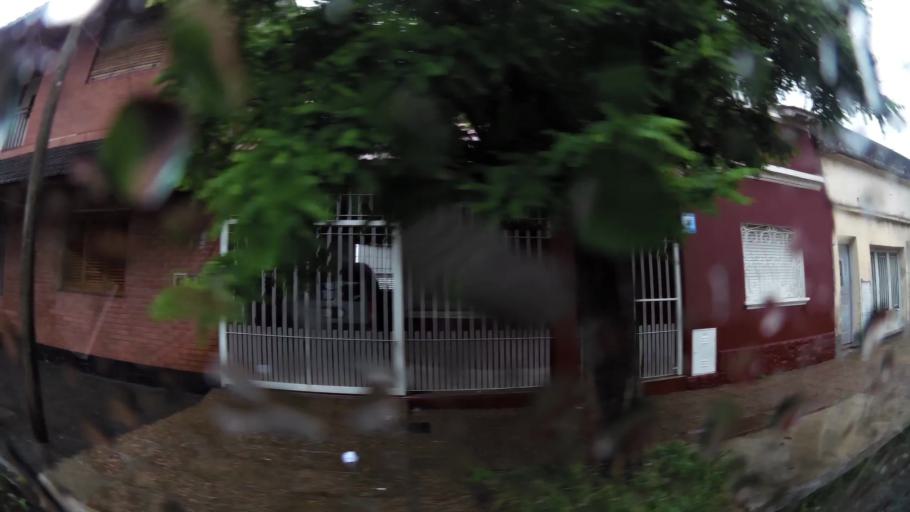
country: AR
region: Buenos Aires
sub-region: Partido de Lanus
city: Lanus
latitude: -34.7232
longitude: -58.4054
